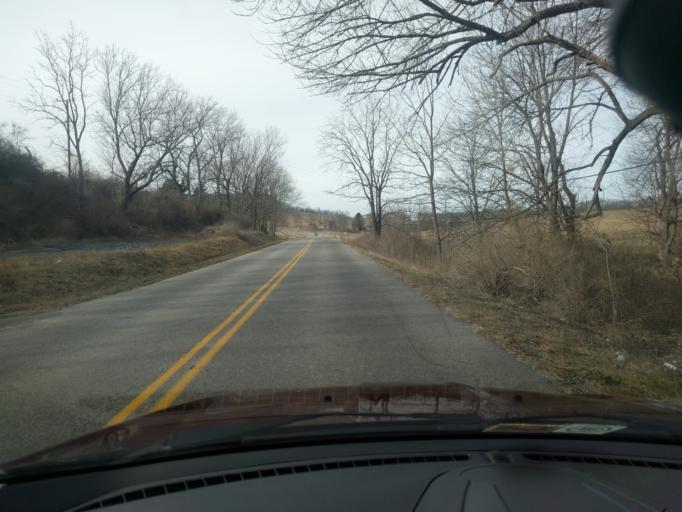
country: US
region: Virginia
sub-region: Augusta County
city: Stuarts Draft
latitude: 37.9286
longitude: -79.2091
